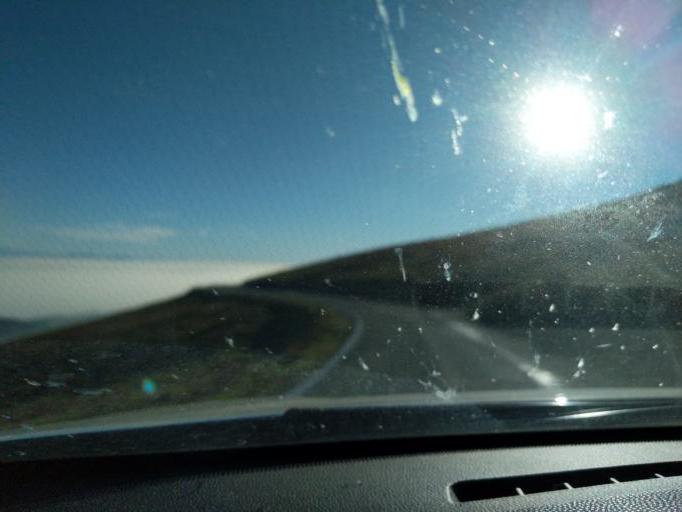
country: CH
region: Bern
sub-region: Jura bernois
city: Saint-Imier
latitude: 47.1232
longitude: 7.0387
